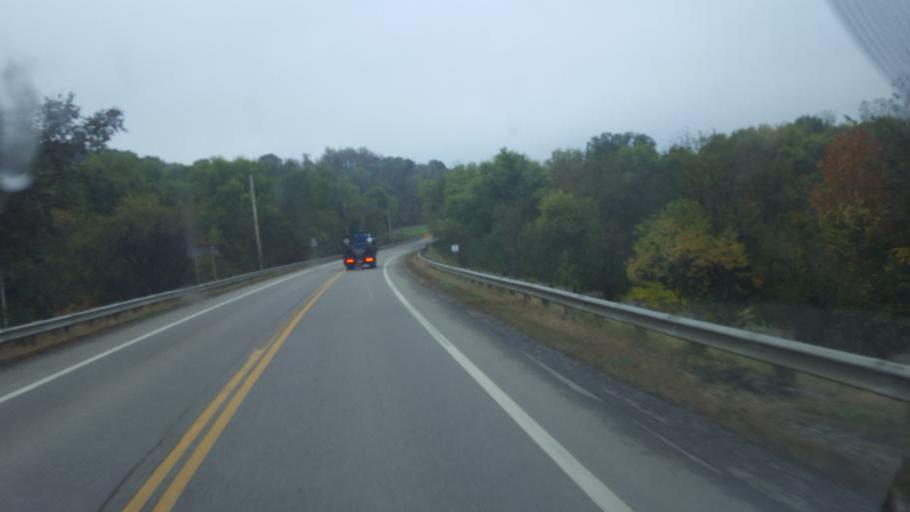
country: US
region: Ohio
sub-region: Tuscarawas County
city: Rockford
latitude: 40.4281
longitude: -81.1901
